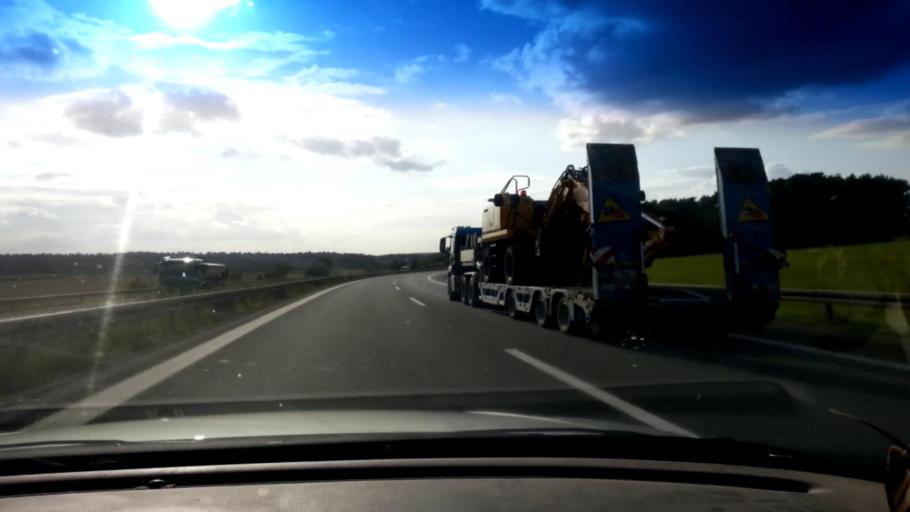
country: DE
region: Bavaria
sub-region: Upper Franconia
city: Wonsees
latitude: 50.0117
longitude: 11.3177
